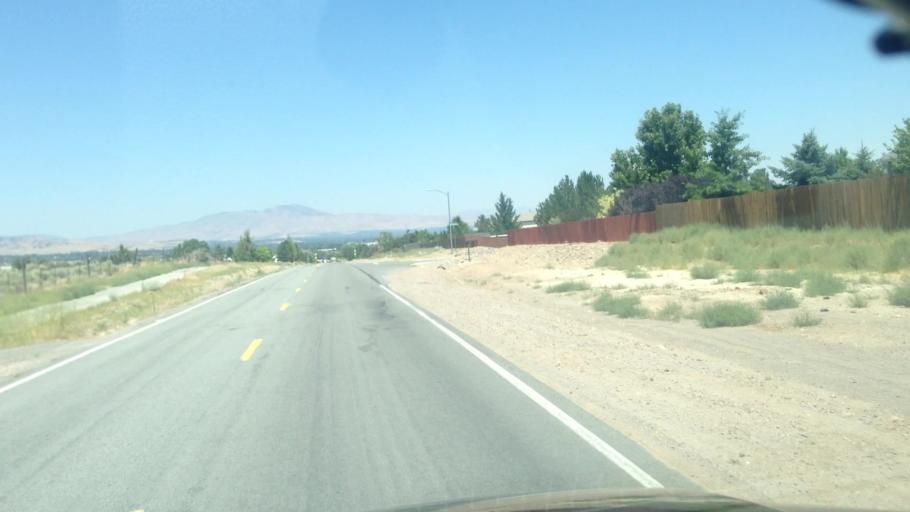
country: US
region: Nevada
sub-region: Storey County
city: Virginia City
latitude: 39.3895
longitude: -119.7291
